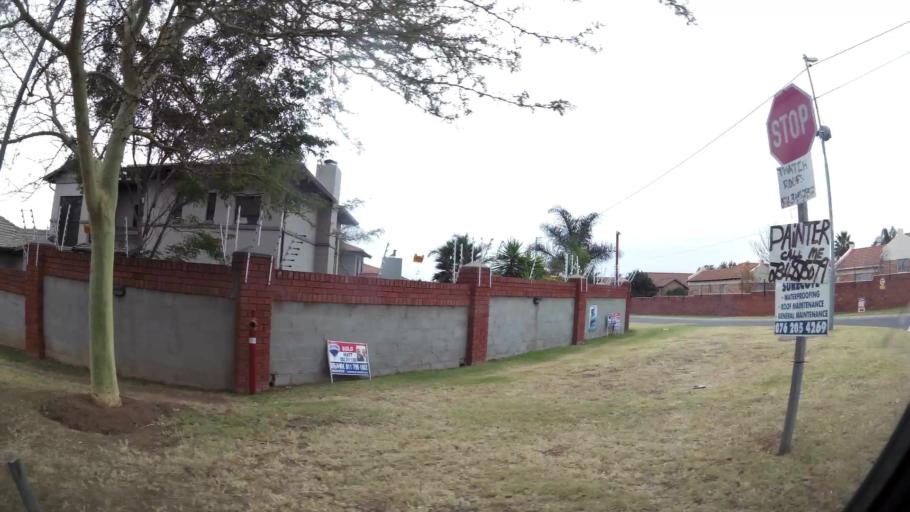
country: ZA
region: Gauteng
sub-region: City of Johannesburg Metropolitan Municipality
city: Roodepoort
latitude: -26.1053
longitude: 27.9020
